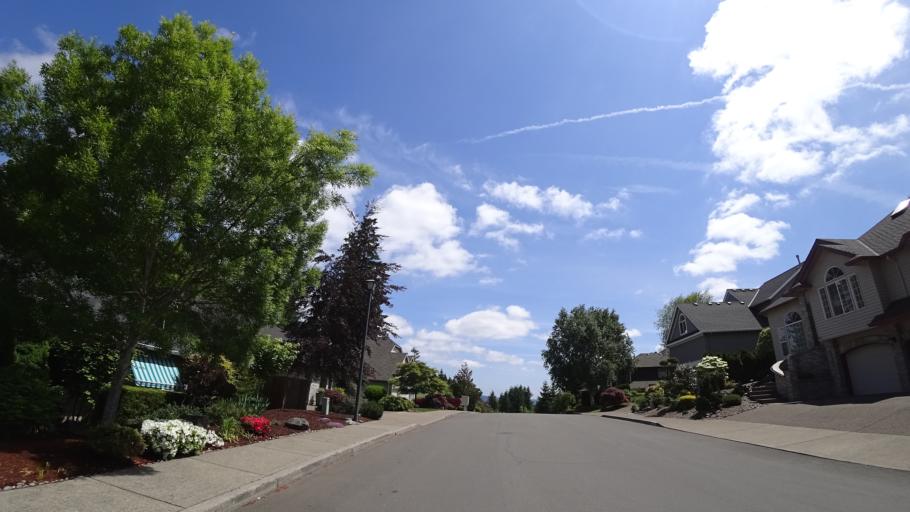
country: US
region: Oregon
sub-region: Washington County
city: King City
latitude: 45.4254
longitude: -122.8185
